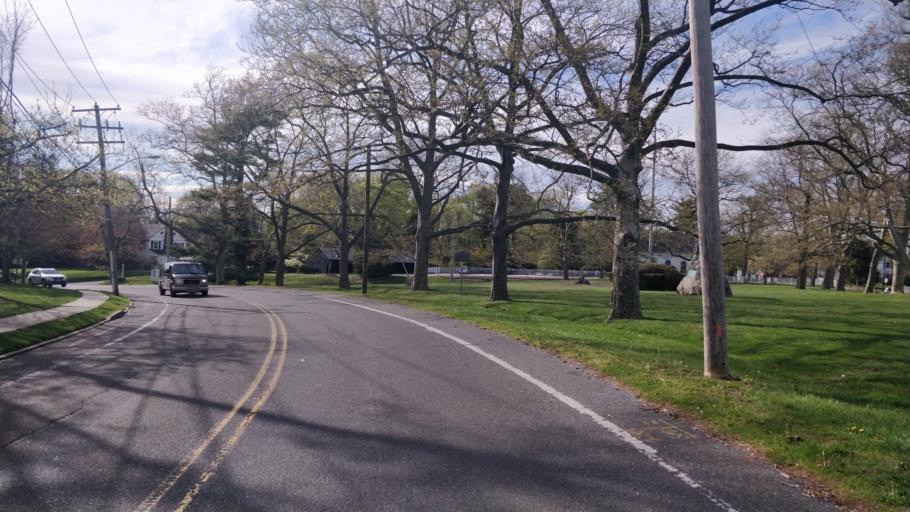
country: US
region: New York
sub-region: Suffolk County
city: East Setauket
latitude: 40.9455
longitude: -73.1113
